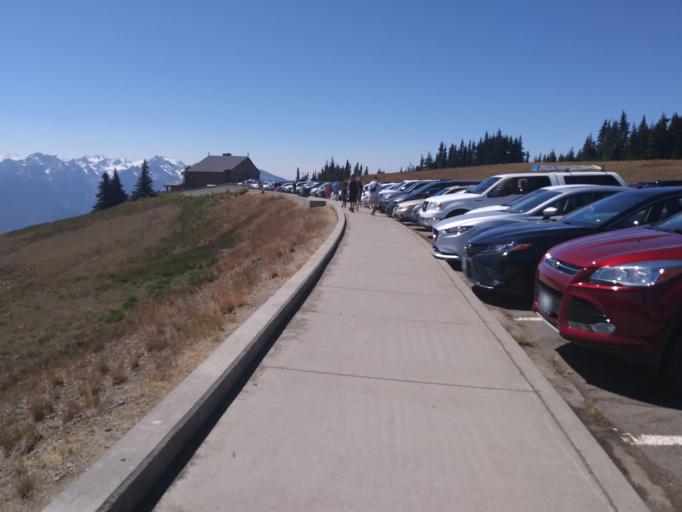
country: US
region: Washington
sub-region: Clallam County
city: Port Angeles
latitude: 47.9700
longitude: -123.4966
